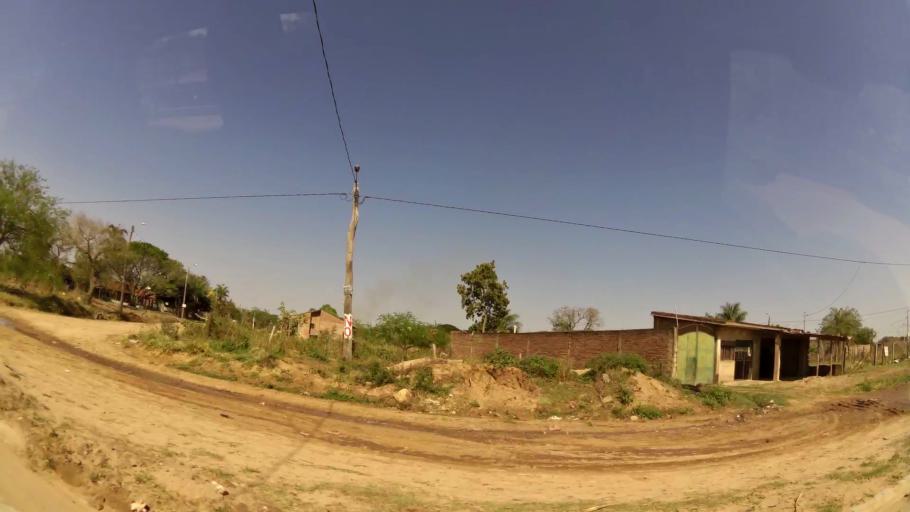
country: BO
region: Santa Cruz
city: Cotoca
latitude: -17.7131
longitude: -63.0667
